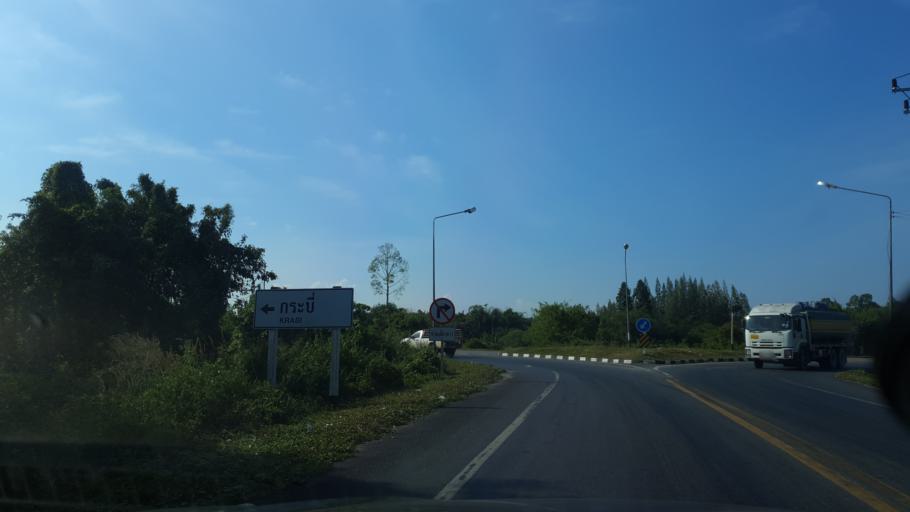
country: TH
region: Surat Thani
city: Ban Na Doem
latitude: 8.9361
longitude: 99.2688
